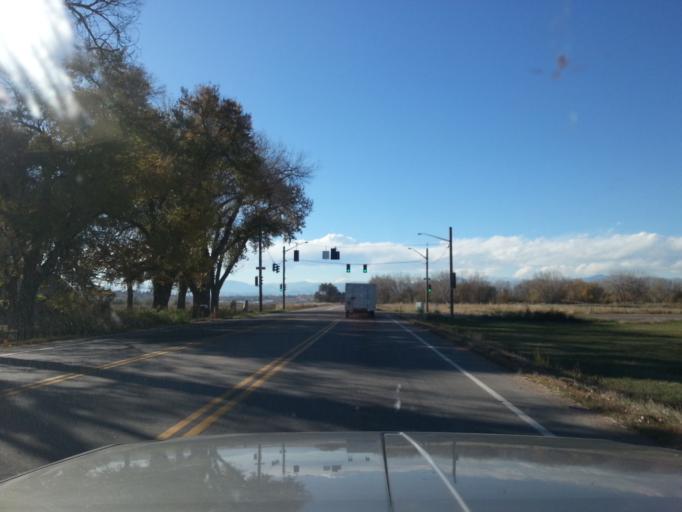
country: US
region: Colorado
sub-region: Larimer County
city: Loveland
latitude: 40.3784
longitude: -105.0535
